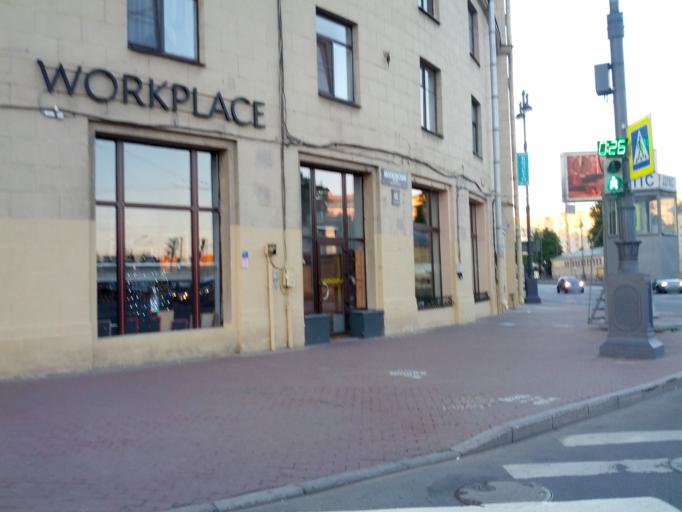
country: RU
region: St.-Petersburg
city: Saint Petersburg
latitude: 59.9083
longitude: 30.3189
